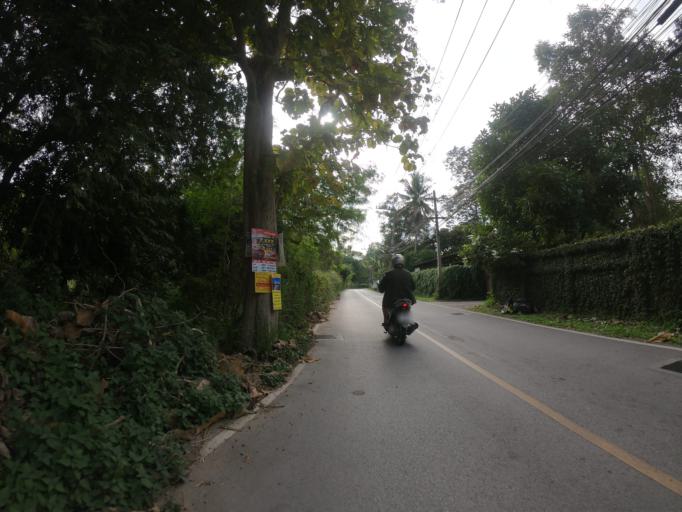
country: TH
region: Chiang Mai
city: Chiang Mai
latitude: 18.8172
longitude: 98.9549
